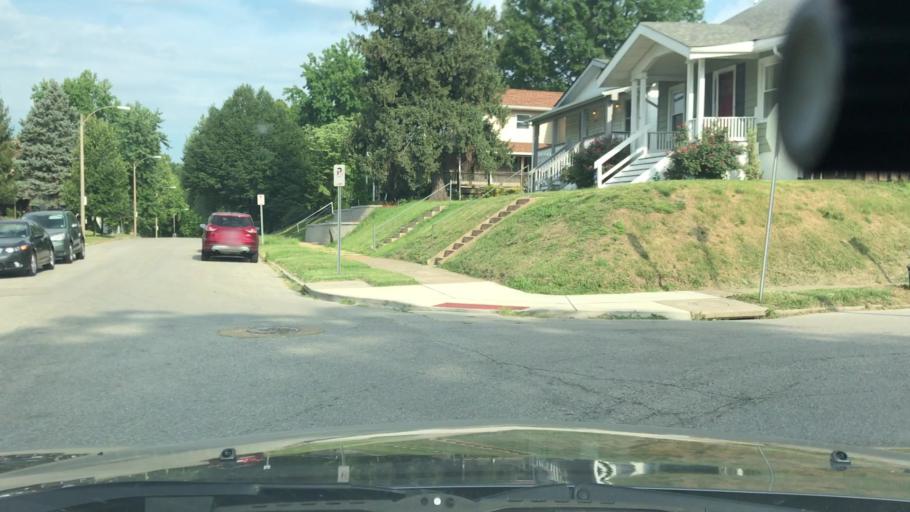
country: US
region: Missouri
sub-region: Saint Louis County
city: Maplewood
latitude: 38.6095
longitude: -90.2968
